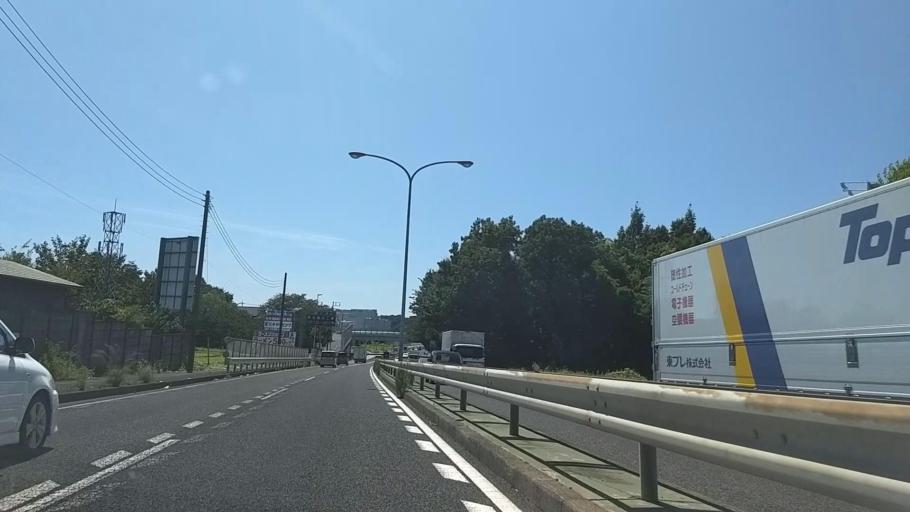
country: JP
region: Kanagawa
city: Zama
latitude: 35.5308
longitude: 139.3625
